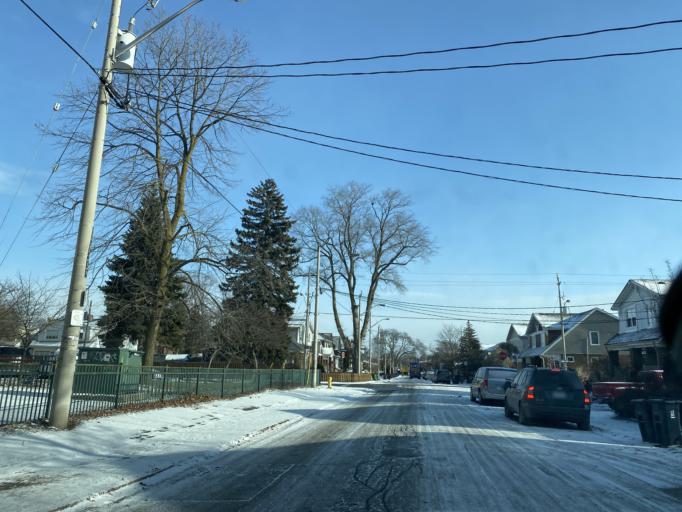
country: CA
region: Ontario
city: Toronto
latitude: 43.6860
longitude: -79.3509
